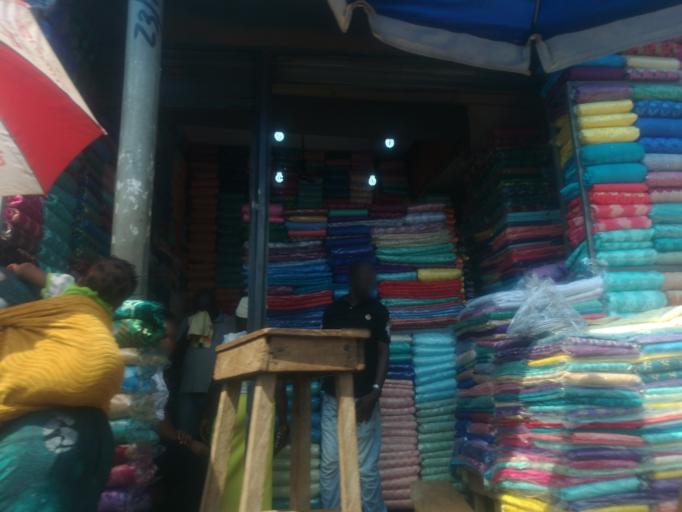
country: NG
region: Oyo
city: Ibadan
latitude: 7.3925
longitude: 3.9561
